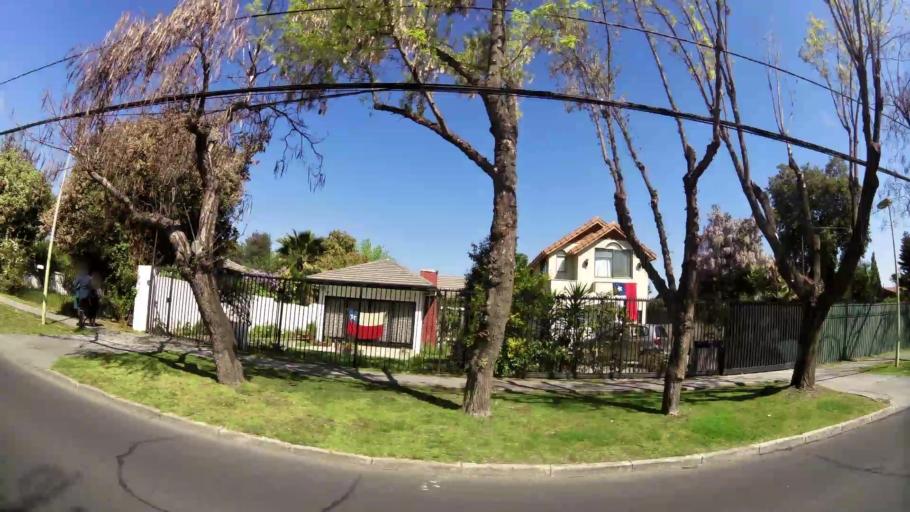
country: CL
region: Santiago Metropolitan
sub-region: Provincia de Santiago
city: Villa Presidente Frei, Nunoa, Santiago, Chile
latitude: -33.4211
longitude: -70.5604
